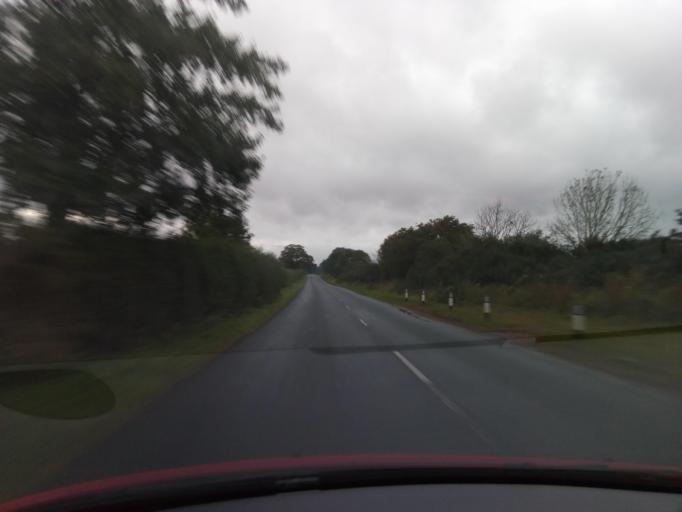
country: GB
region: England
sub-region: Darlington
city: High Coniscliffe
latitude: 54.5106
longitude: -1.6713
